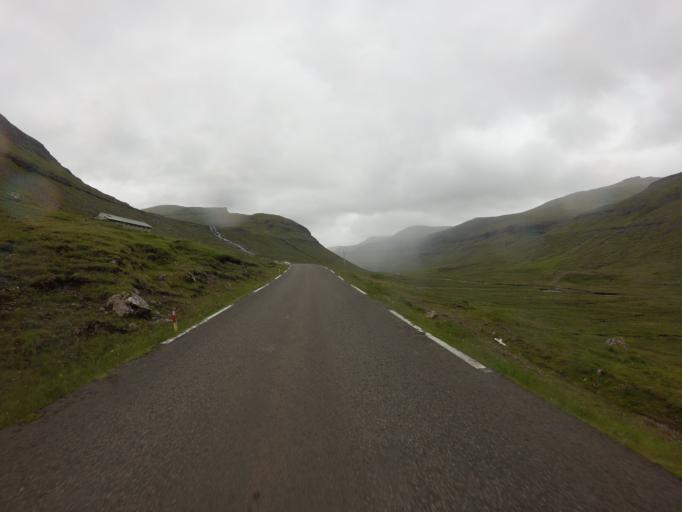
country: FO
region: Streymoy
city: Vestmanna
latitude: 62.2182
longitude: -7.1226
